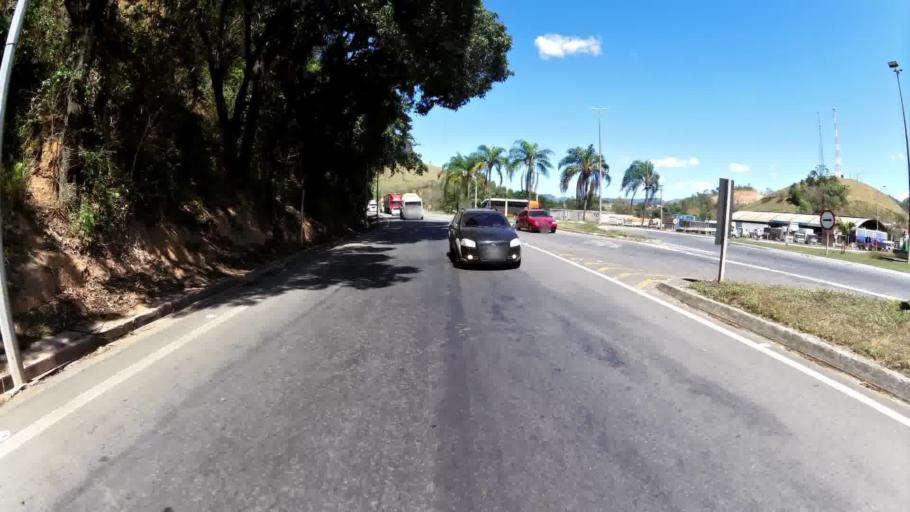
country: BR
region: Espirito Santo
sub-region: Viana
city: Viana
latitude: -20.3852
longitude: -40.4621
